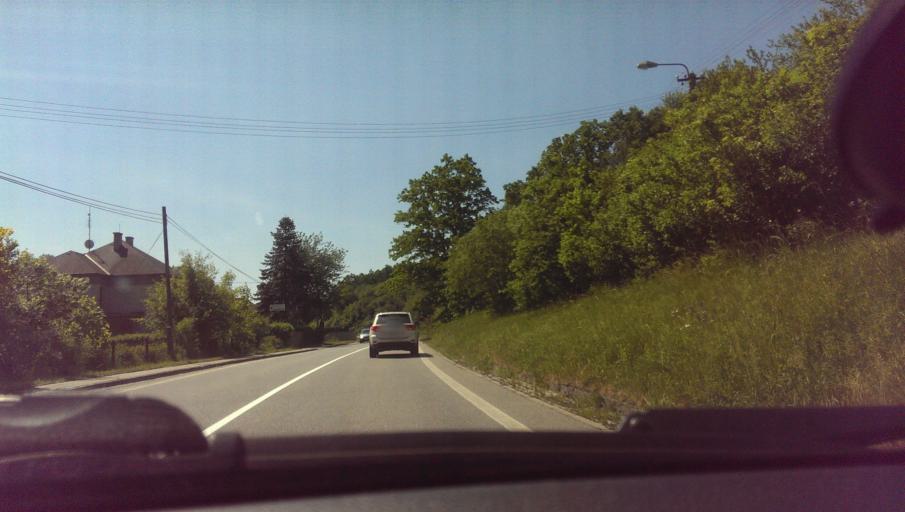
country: CZ
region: Zlin
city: Brezolupy
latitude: 49.1439
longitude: 17.6054
